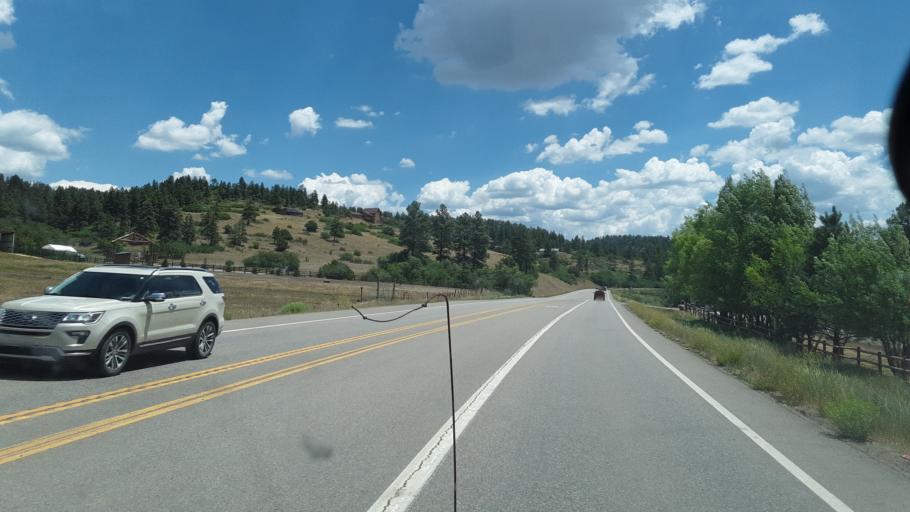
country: US
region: Colorado
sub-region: Archuleta County
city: Pagosa Springs
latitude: 37.2411
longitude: -107.1471
